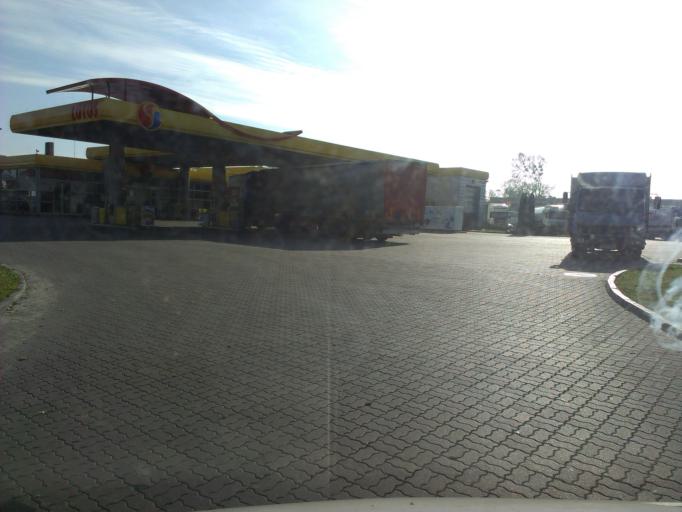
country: PL
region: West Pomeranian Voivodeship
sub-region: Powiat gryfinski
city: Stare Czarnowo
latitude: 53.3622
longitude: 14.7411
